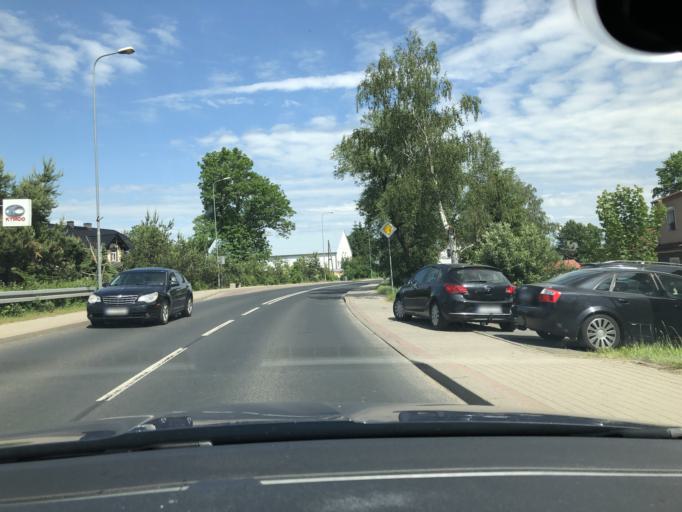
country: PL
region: Lower Silesian Voivodeship
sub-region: Powiat jeleniogorski
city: Jezow Sudecki
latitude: 50.9115
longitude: 15.8182
